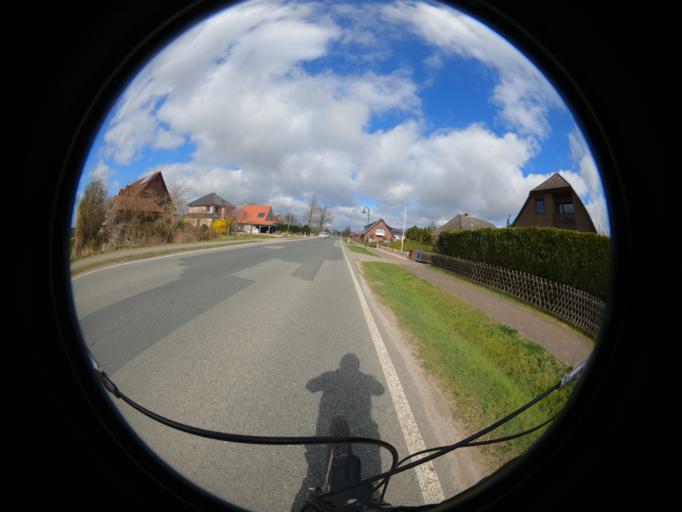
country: DE
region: Lower Saxony
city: Neu Wulmstorf
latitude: 53.4940
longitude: 9.7797
